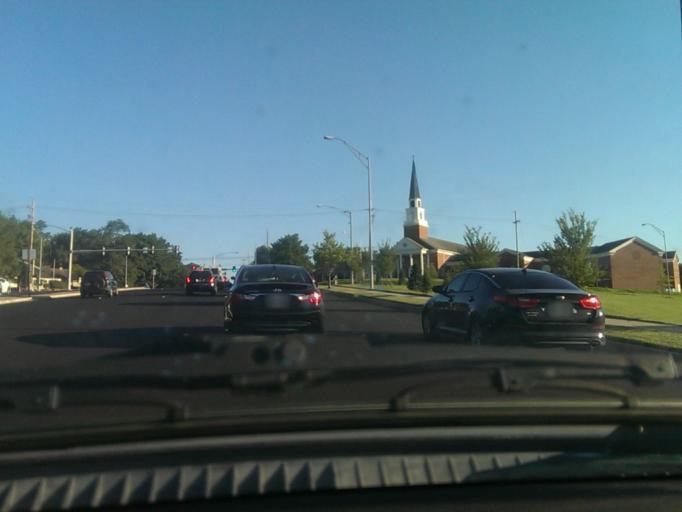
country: US
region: Kansas
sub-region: Johnson County
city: Leawood
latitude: 38.9572
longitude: -94.5960
